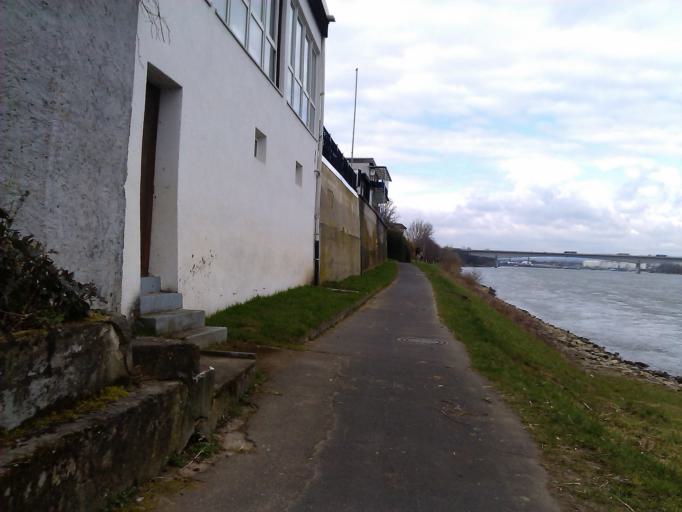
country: DE
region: Rheinland-Pfalz
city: Sankt Sebastian
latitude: 50.4010
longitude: 7.5815
